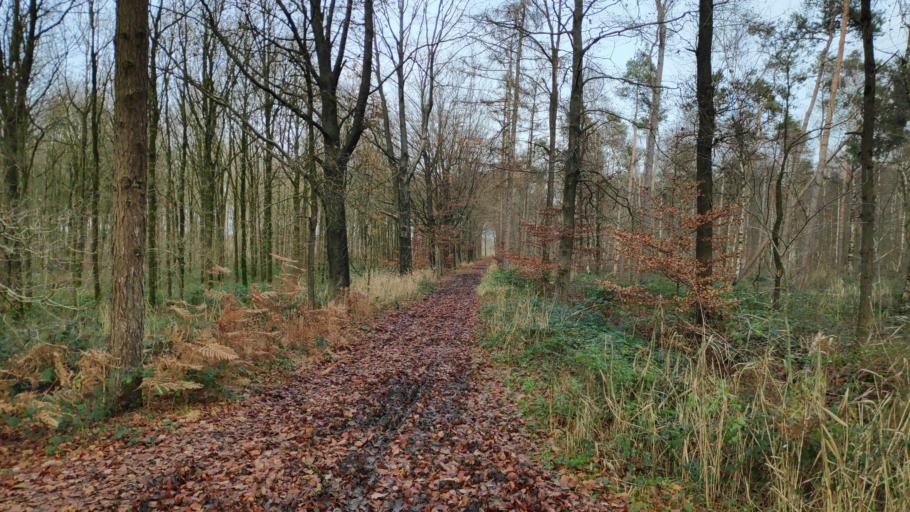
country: BE
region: Flanders
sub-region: Provincie Oost-Vlaanderen
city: Knesselare
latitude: 51.1600
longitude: 3.4437
